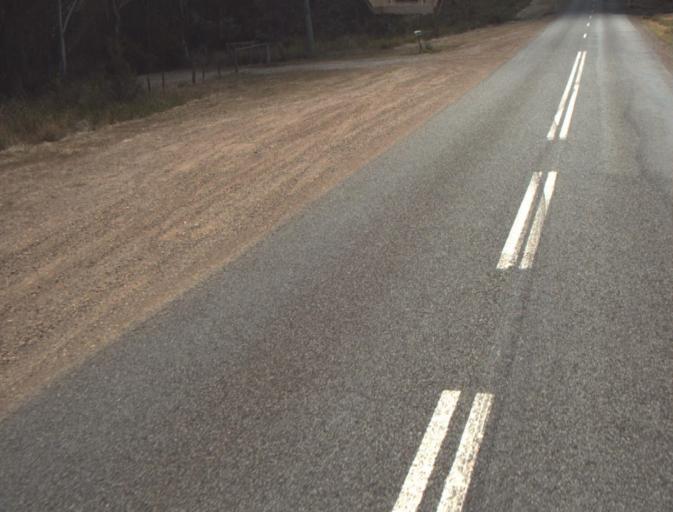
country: AU
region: Tasmania
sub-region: Launceston
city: Mayfield
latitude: -41.3133
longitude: 147.1348
